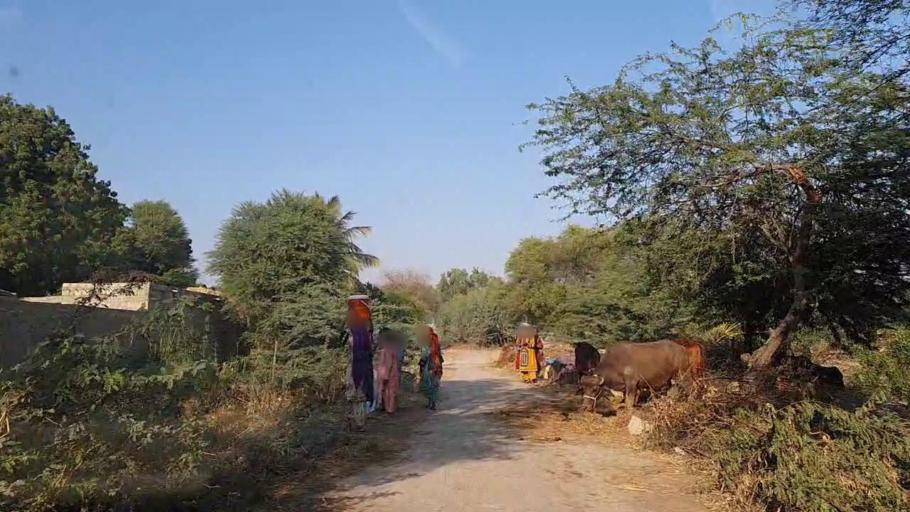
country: PK
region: Sindh
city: Thatta
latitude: 24.7673
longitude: 67.9666
